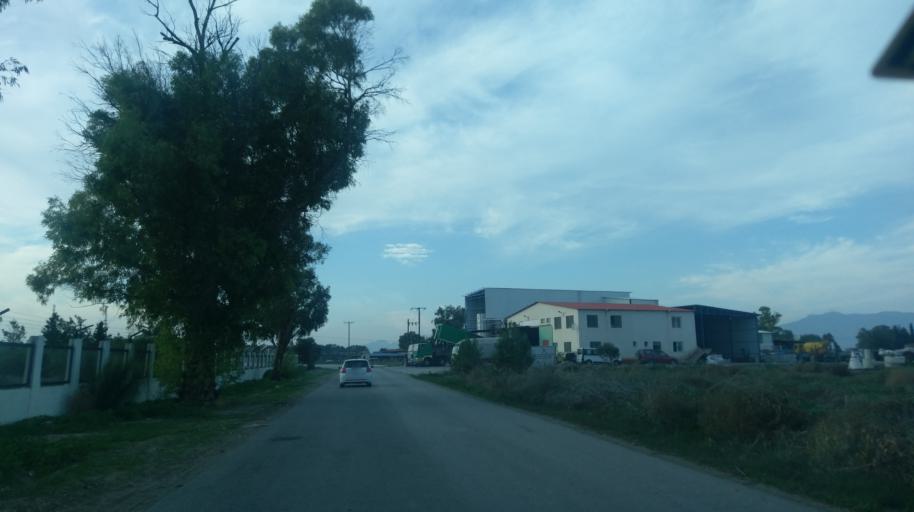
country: CY
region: Larnaka
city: Athienou
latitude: 35.1578
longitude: 33.6177
